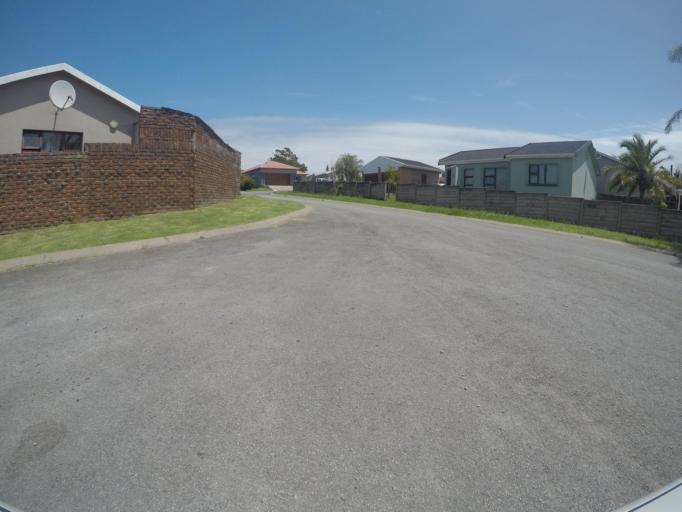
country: ZA
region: Eastern Cape
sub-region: Buffalo City Metropolitan Municipality
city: East London
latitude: -32.9371
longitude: 27.9918
